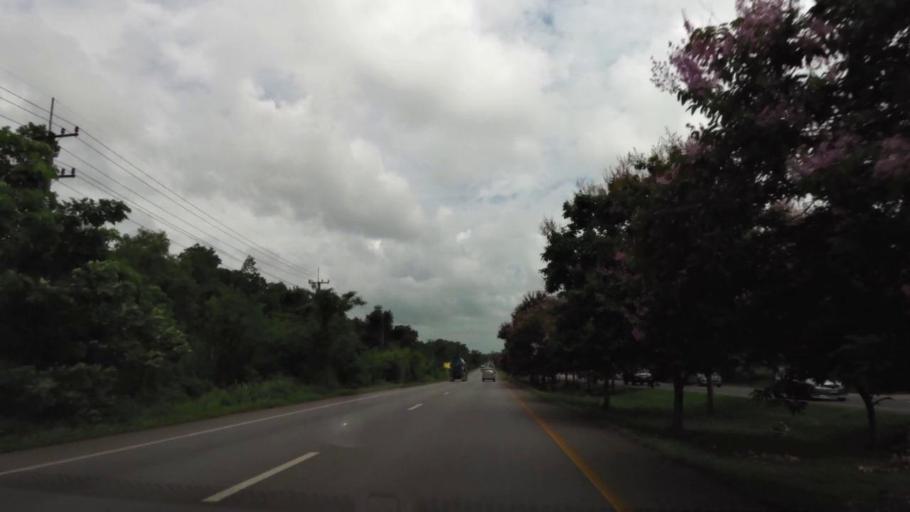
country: TH
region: Chanthaburi
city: Na Yai Am
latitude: 12.7464
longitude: 101.8809
